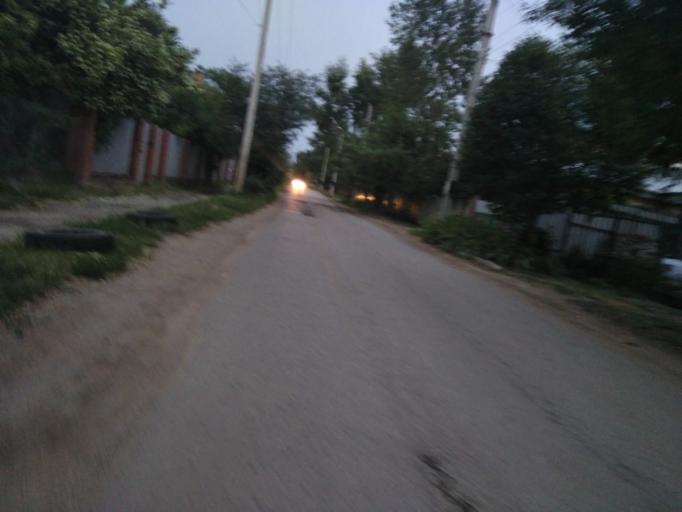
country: RU
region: Tula
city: Lomintsevskiy
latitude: 53.9332
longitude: 37.6224
